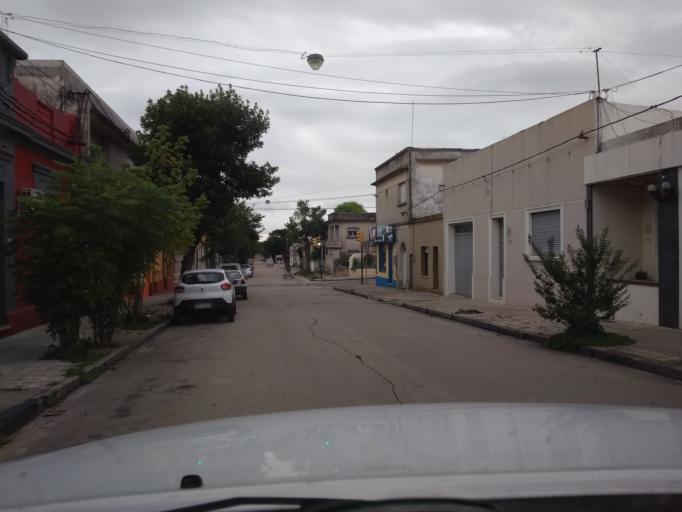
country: UY
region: Florida
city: Florida
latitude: -34.0989
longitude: -56.2176
